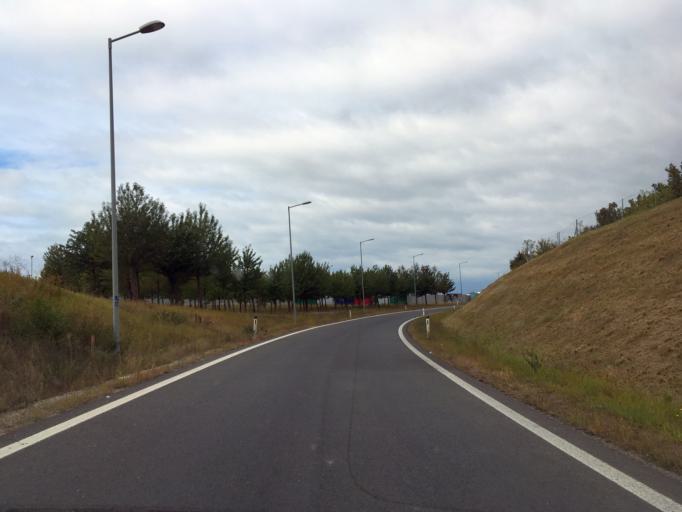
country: AT
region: Lower Austria
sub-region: Politischer Bezirk Modling
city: Vosendorf
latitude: 48.1329
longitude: 16.3422
